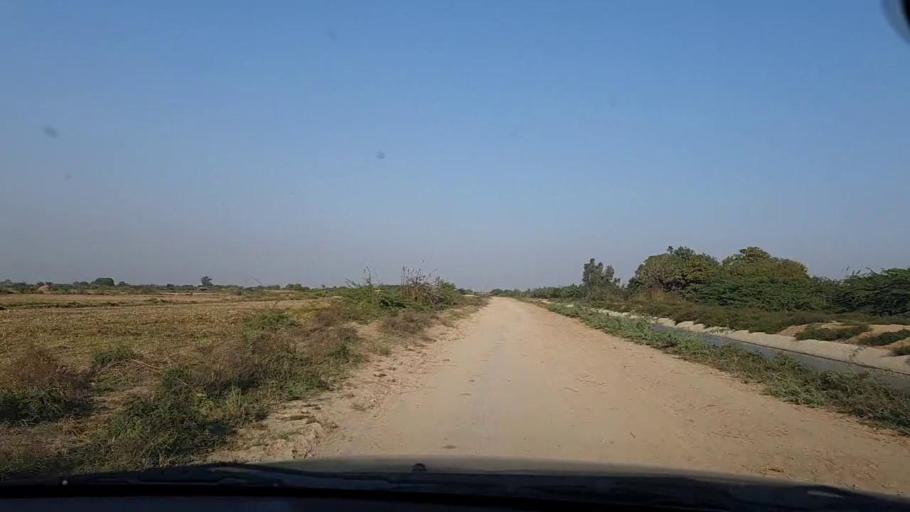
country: PK
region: Sindh
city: Chuhar Jamali
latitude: 24.2879
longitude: 67.7511
